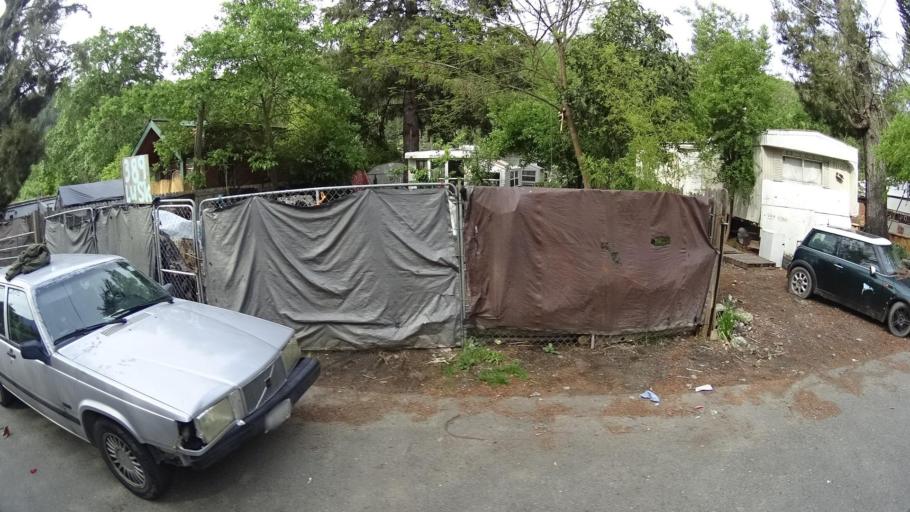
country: US
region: California
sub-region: Humboldt County
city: Redway
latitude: 40.2081
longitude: -123.7896
